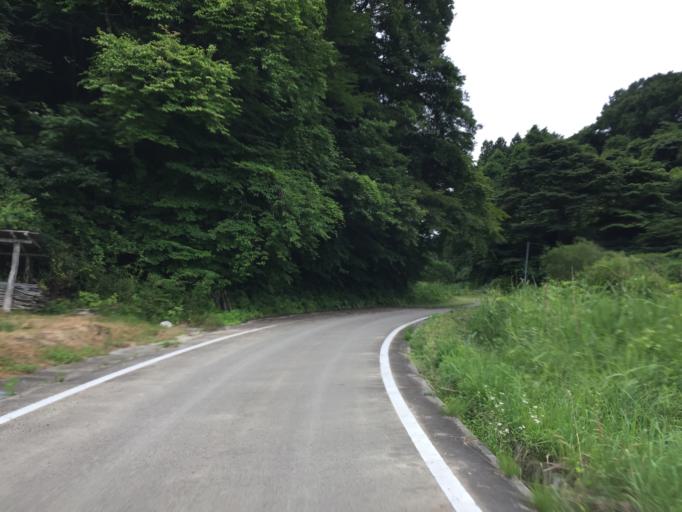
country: JP
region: Fukushima
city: Ishikawa
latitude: 37.2047
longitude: 140.6022
